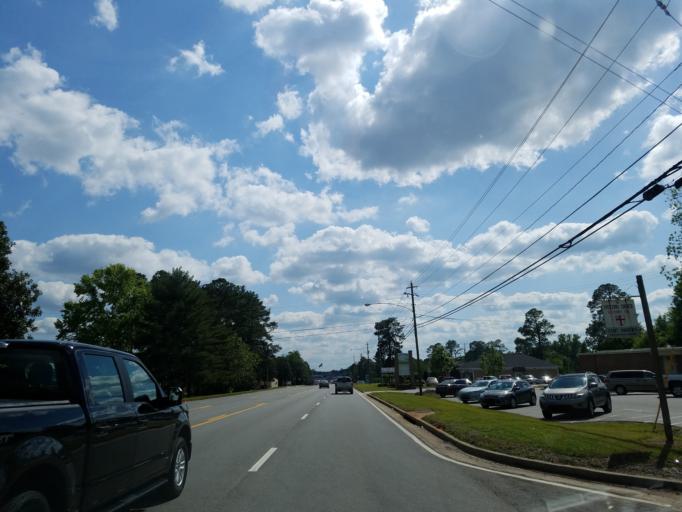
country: US
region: Georgia
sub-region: Peach County
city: Fort Valley
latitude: 32.5676
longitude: -83.8755
